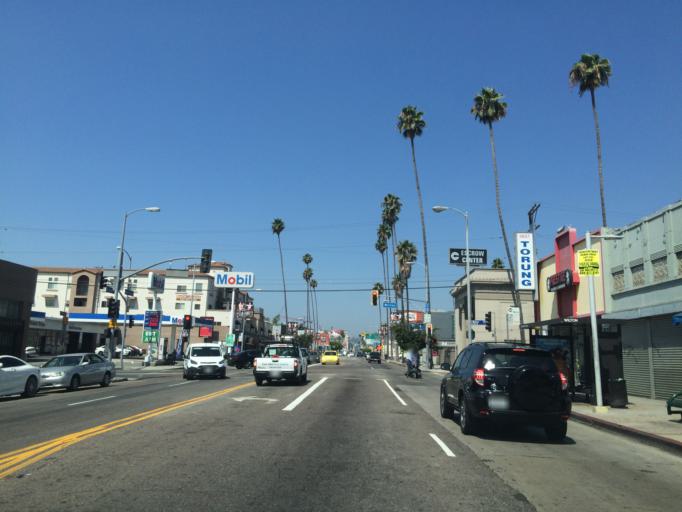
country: US
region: California
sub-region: Los Angeles County
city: Hollywood
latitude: 34.1018
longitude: -118.3132
